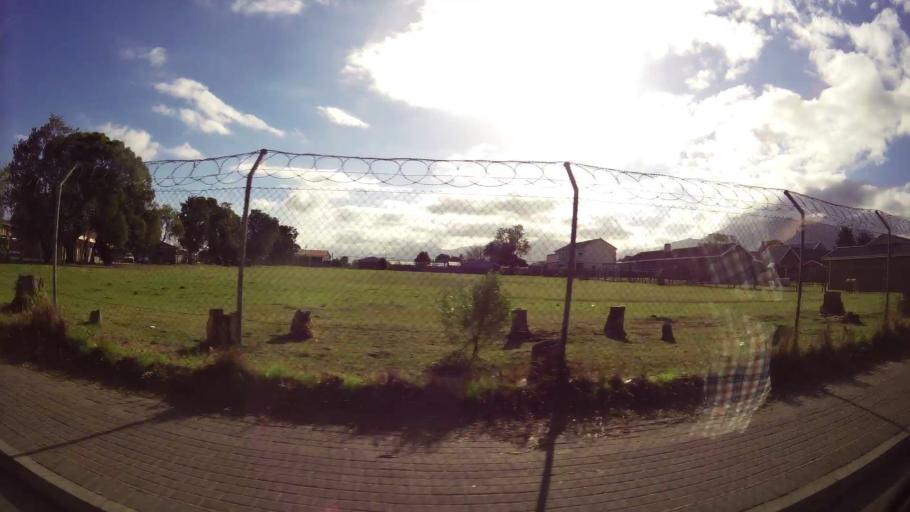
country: ZA
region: Western Cape
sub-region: Eden District Municipality
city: George
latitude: -33.9751
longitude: 22.4794
